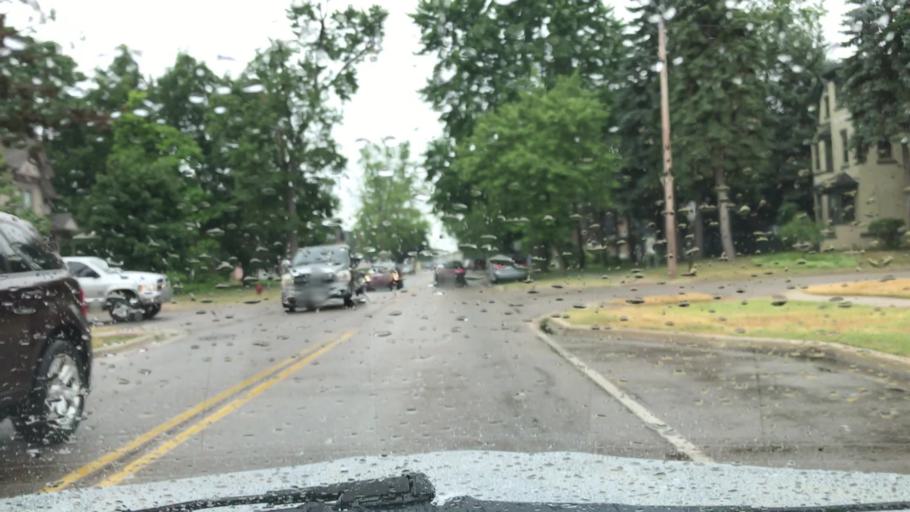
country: US
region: Michigan
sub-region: Macomb County
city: Utica
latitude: 42.6289
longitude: -83.0345
